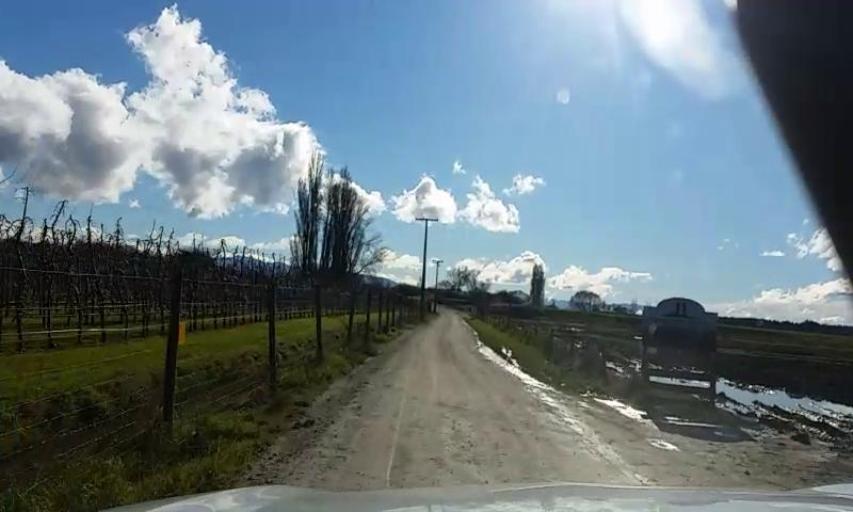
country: NZ
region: Tasman
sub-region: Tasman District
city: Richmond
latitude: -41.3005
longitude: 173.1418
